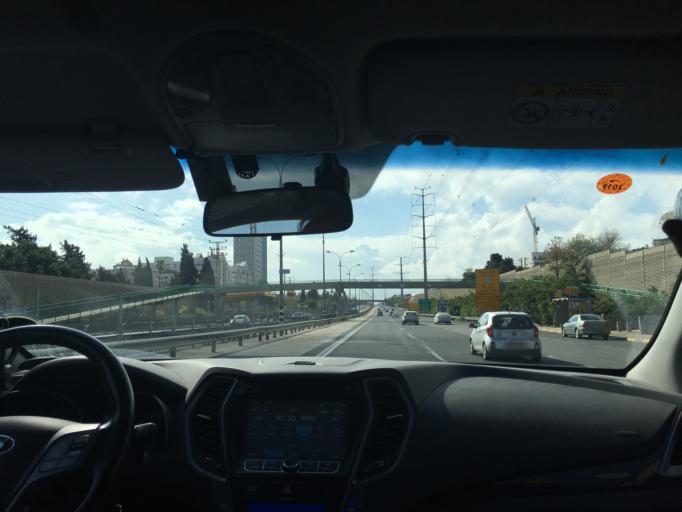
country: IL
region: Tel Aviv
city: Giv`at Shemu'el
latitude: 32.0833
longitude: 34.8453
